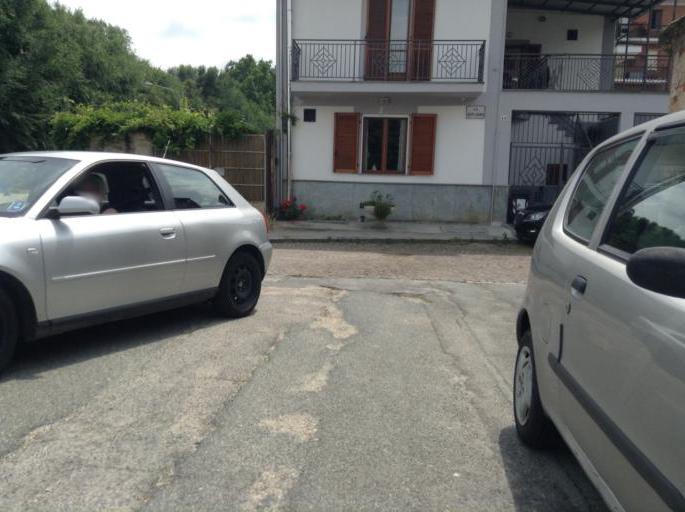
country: IT
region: Piedmont
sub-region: Provincia di Torino
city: Carignano
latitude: 44.9057
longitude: 7.6777
